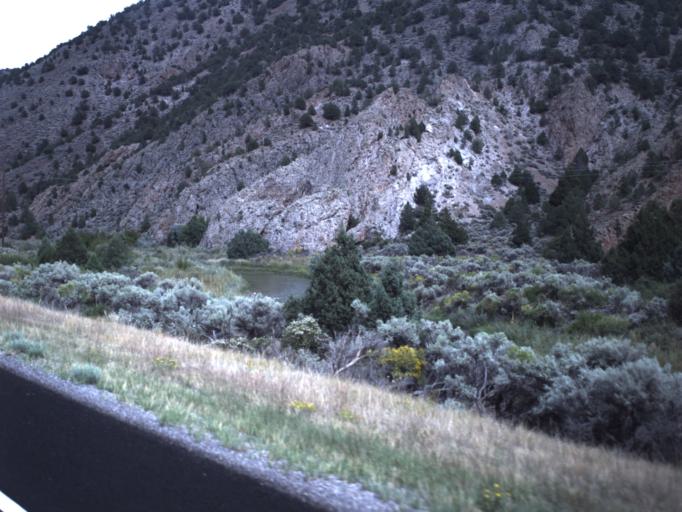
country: US
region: Utah
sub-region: Piute County
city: Junction
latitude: 38.0879
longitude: -112.3392
